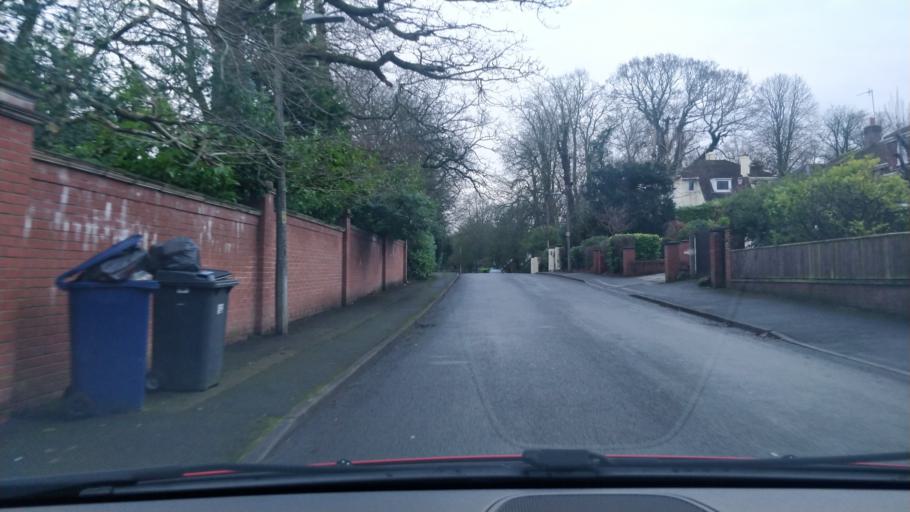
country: GB
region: England
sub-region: Lancashire
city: Preston
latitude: 53.7477
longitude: -2.7239
